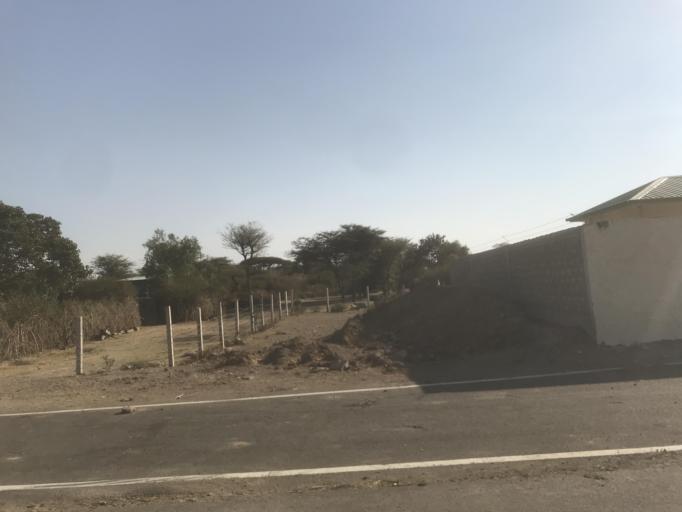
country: ET
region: Oromiya
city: Mojo
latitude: 8.3006
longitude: 38.9388
